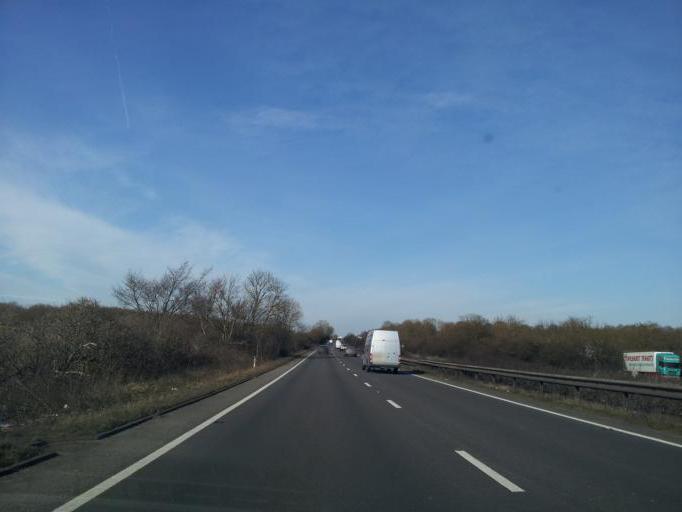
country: GB
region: England
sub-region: District of Rutland
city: Clipsham
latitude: 52.7135
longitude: -0.5930
